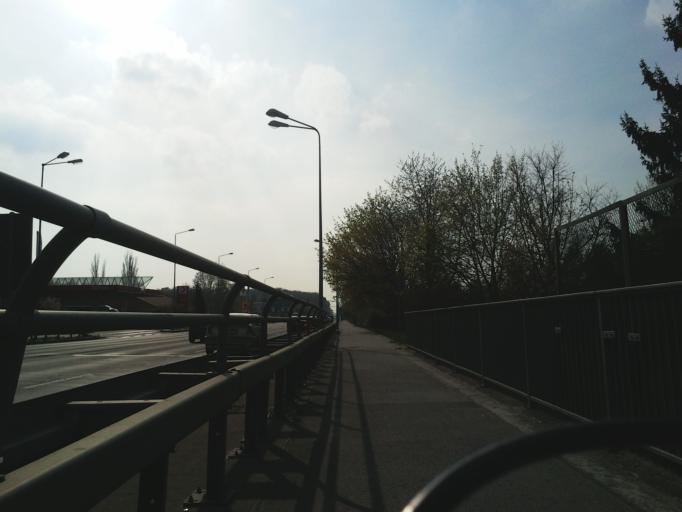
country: DE
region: Mecklenburg-Vorpommern
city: Roggentin
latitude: 54.0811
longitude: 12.1906
